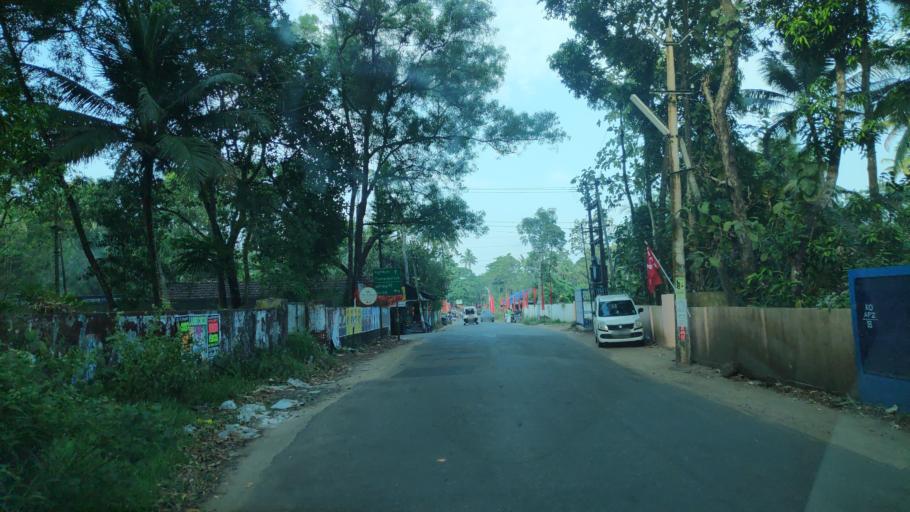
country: IN
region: Kerala
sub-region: Alappuzha
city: Shertallai
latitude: 9.6028
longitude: 76.3588
